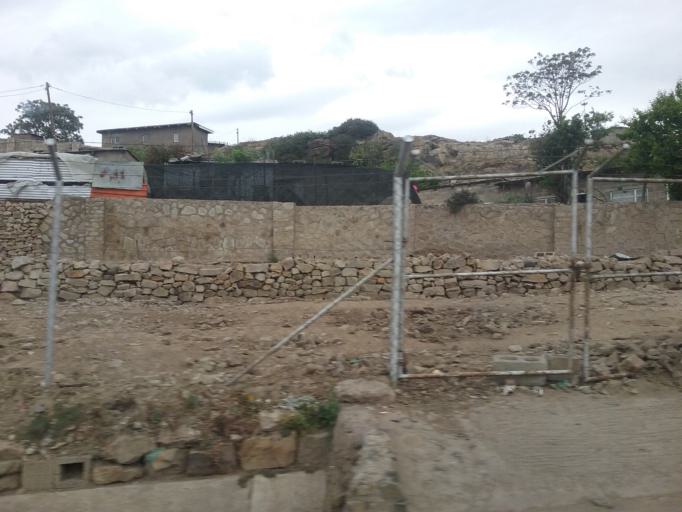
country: LS
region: Maseru
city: Maseru
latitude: -29.3242
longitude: 27.5086
